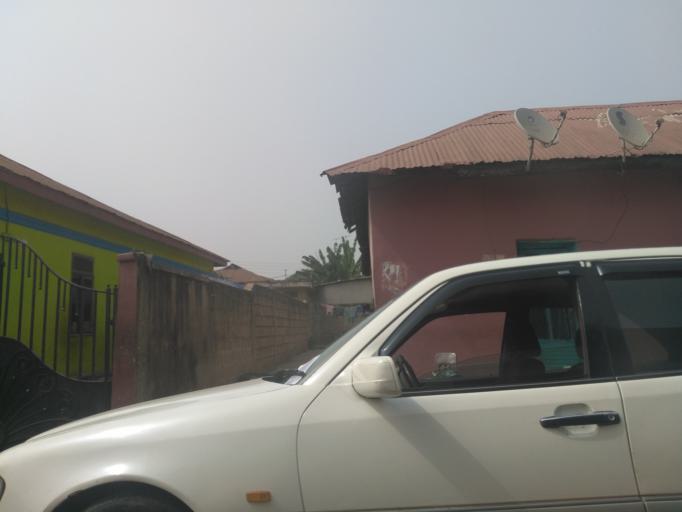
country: GH
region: Ashanti
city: Kumasi
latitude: 6.7060
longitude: -1.6216
